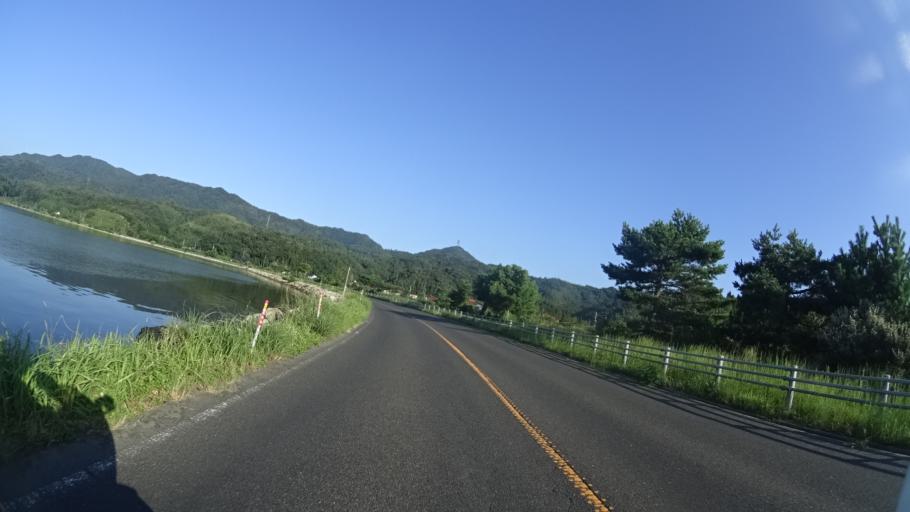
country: JP
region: Shimane
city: Sakaiminato
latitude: 35.5360
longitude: 133.1605
